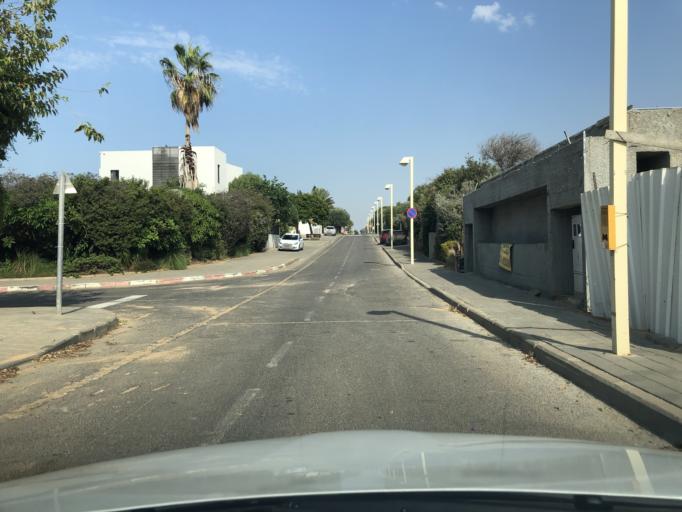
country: IL
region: Tel Aviv
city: Kefar Shemaryahu
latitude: 32.2133
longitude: 34.8170
